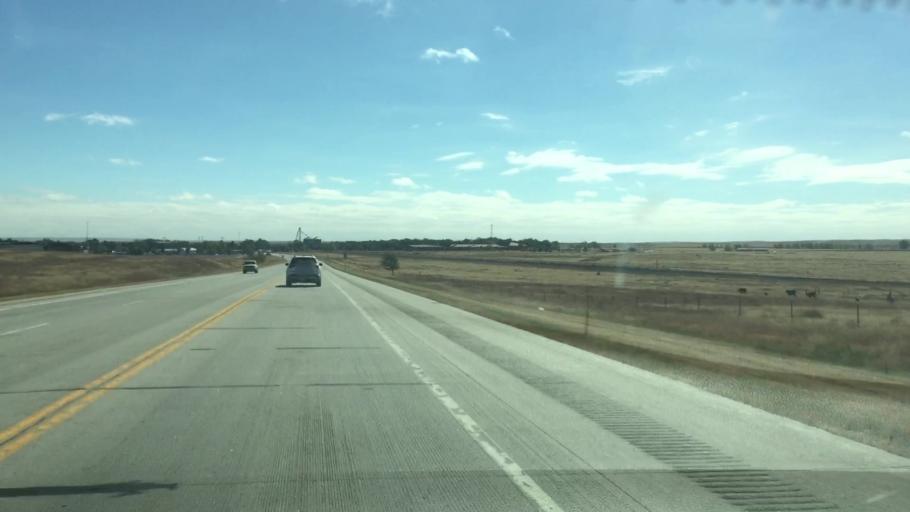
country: US
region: Colorado
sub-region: Lincoln County
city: Hugo
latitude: 39.1403
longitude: -103.4855
